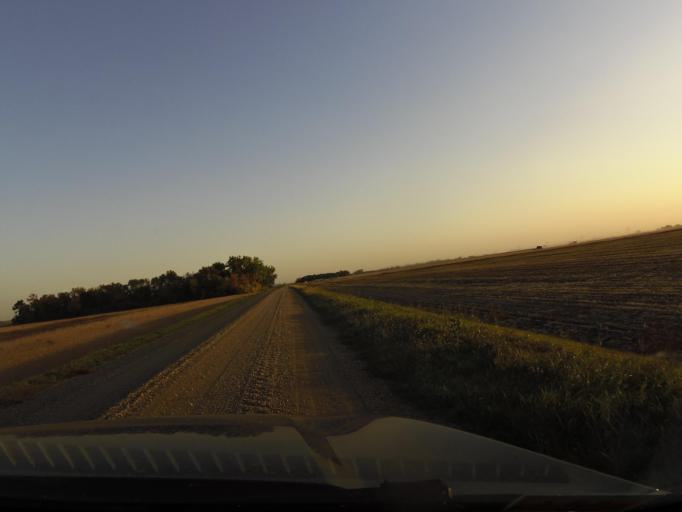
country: US
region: North Dakota
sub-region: Walsh County
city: Grafton
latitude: 48.3926
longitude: -97.2556
